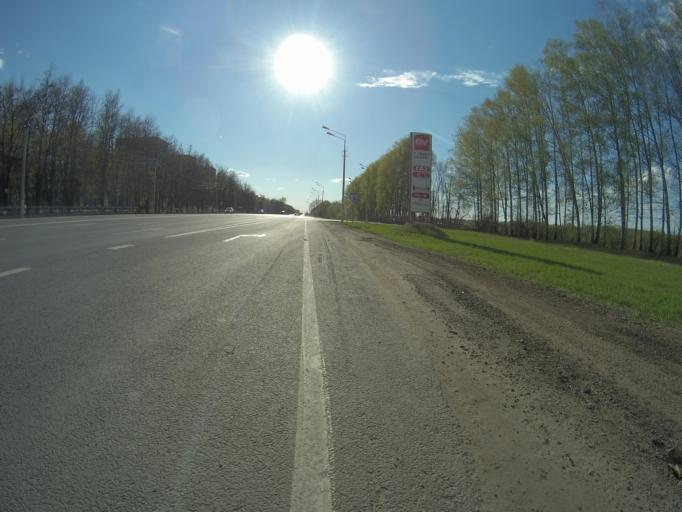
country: RU
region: Vladimir
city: Bogolyubovo
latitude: 56.1748
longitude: 40.4811
